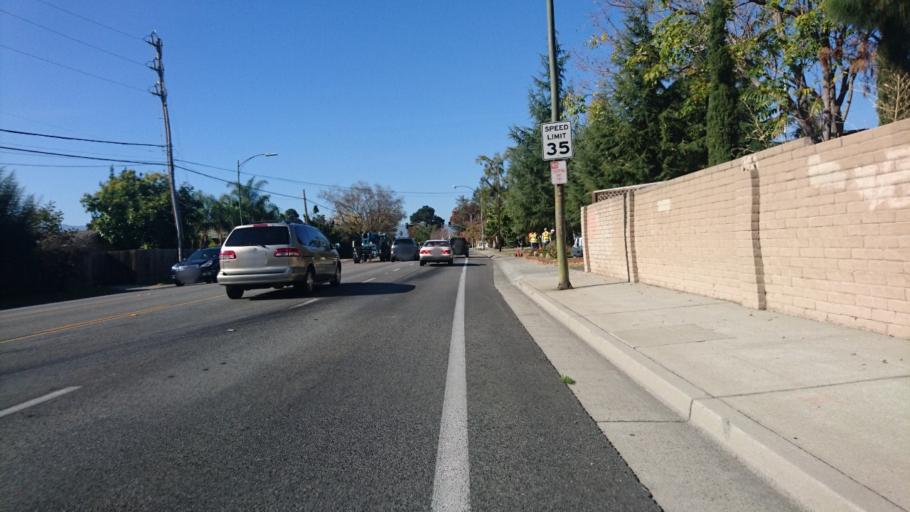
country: US
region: California
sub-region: Santa Clara County
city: Campbell
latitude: 37.2869
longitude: -121.9653
